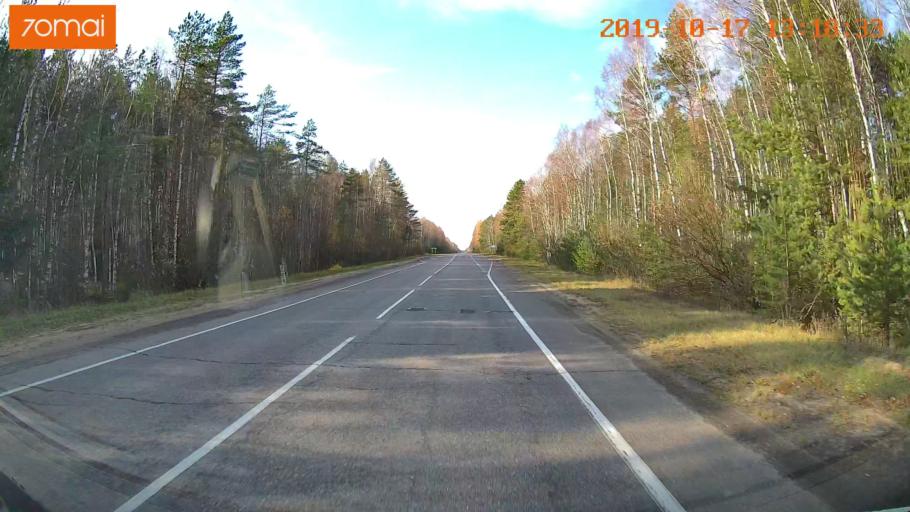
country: RU
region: Rjazan
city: Gus'-Zheleznyy
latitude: 55.0637
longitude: 41.0953
